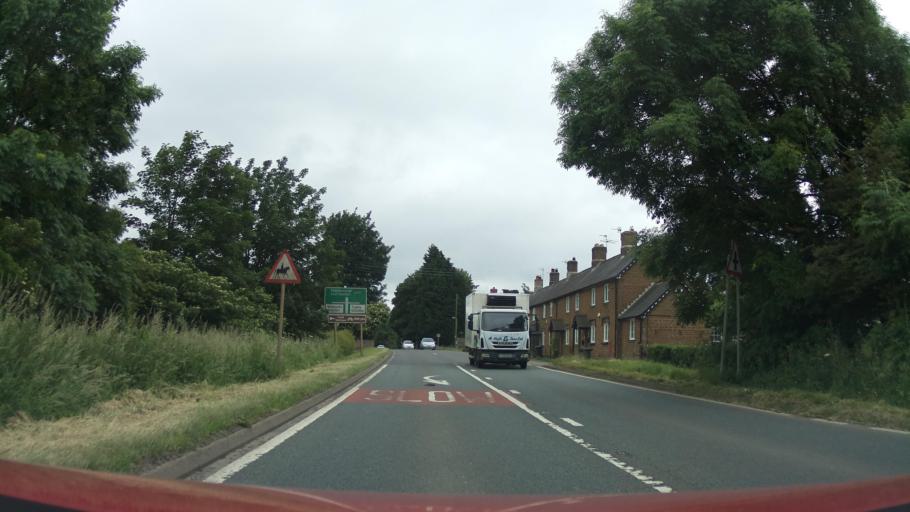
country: GB
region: England
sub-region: Leicestershire
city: Houghton on the Hill
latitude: 52.6038
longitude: -0.8770
